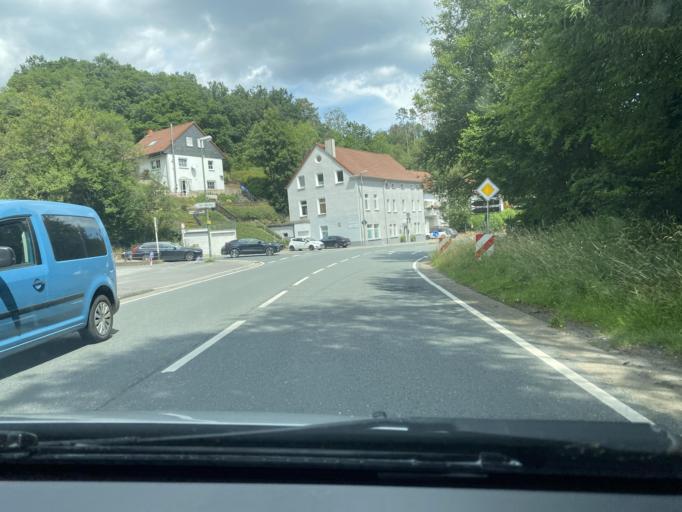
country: DE
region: North Rhine-Westphalia
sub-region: Regierungsbezirk Arnsberg
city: Luedenscheid
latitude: 51.2547
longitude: 7.6315
